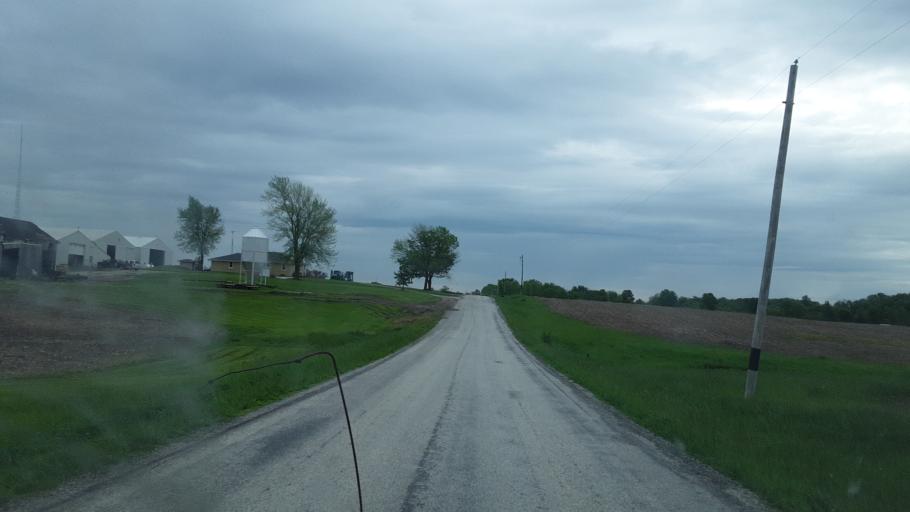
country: US
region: Illinois
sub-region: McDonough County
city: Macomb
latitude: 40.3816
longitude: -90.6143
